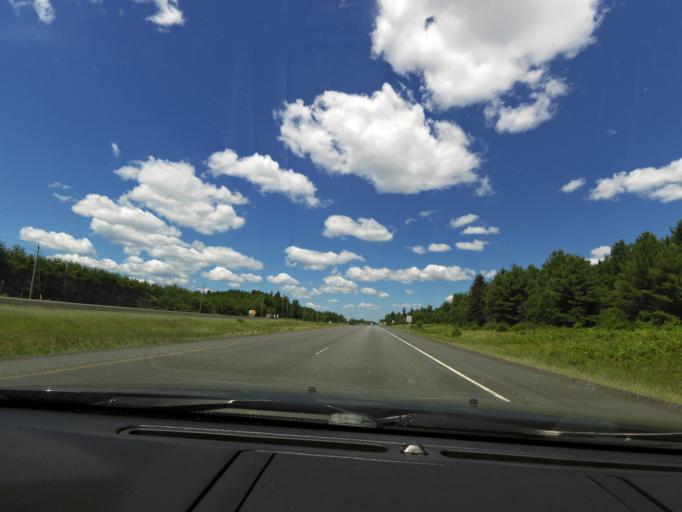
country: CA
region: Ontario
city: Huntsville
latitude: 45.4843
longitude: -79.2804
